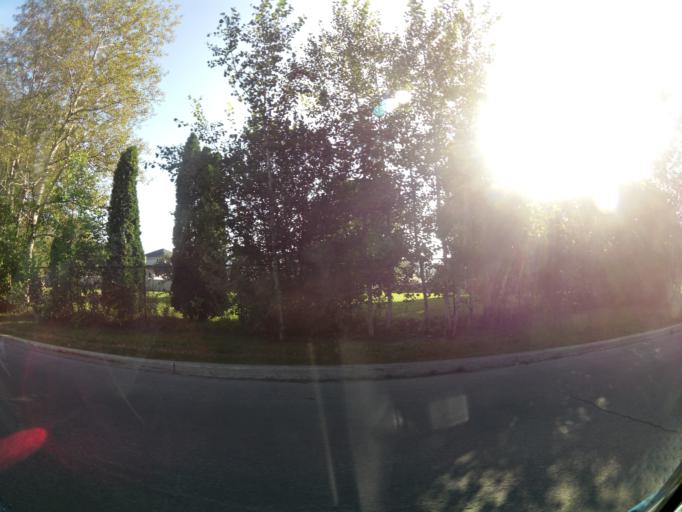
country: CA
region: Ontario
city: Clarence-Rockland
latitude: 45.4828
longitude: -75.4766
